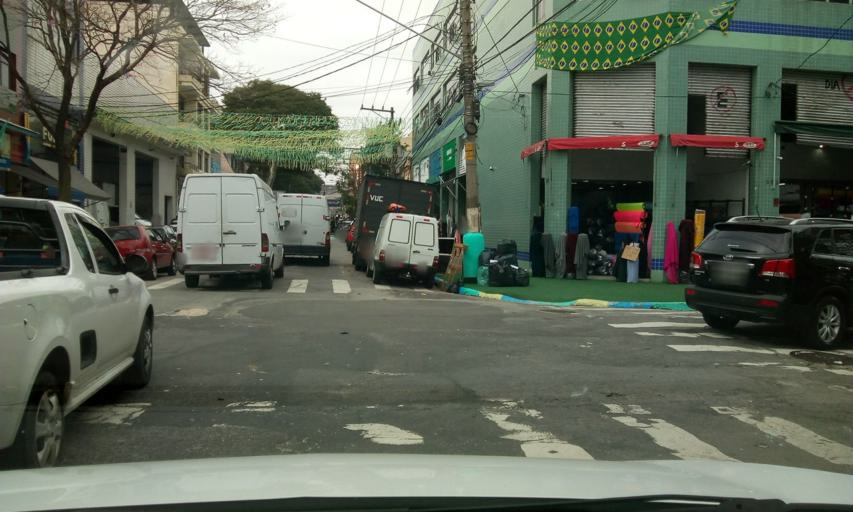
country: BR
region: Sao Paulo
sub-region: Sao Paulo
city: Sao Paulo
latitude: -23.5336
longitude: -46.6083
